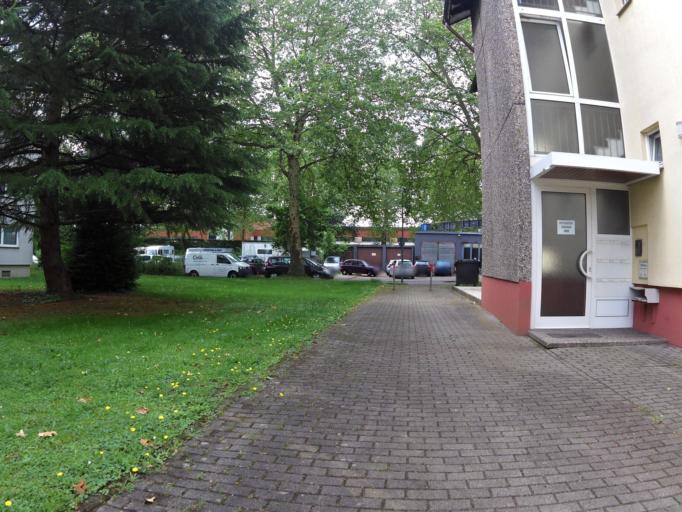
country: DE
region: Baden-Wuerttemberg
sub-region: Freiburg Region
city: Lahr
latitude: 48.3453
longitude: 7.8348
